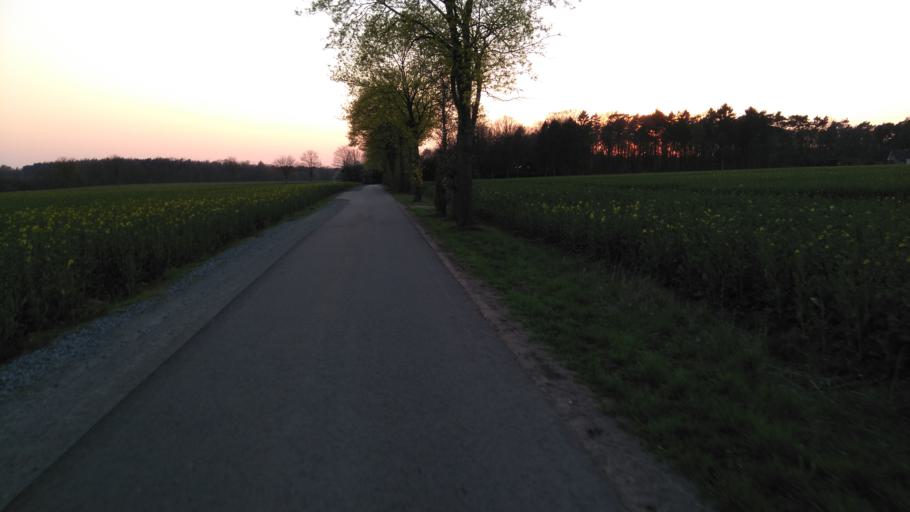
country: DE
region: Lower Saxony
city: Bargstedt
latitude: 53.4478
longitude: 9.4618
